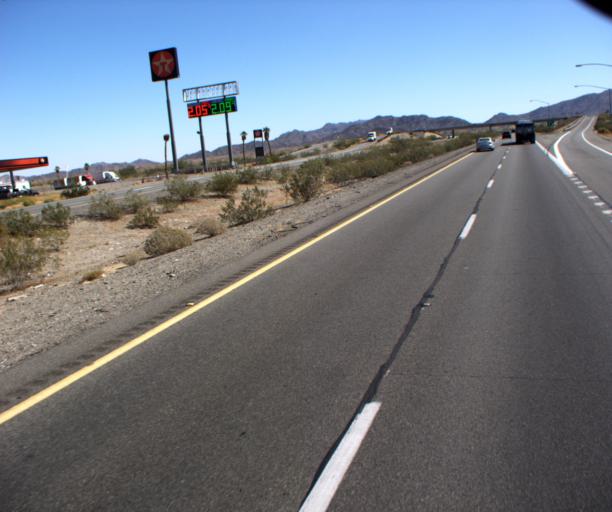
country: US
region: Arizona
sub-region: La Paz County
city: Ehrenberg
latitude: 33.6230
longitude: -114.4379
